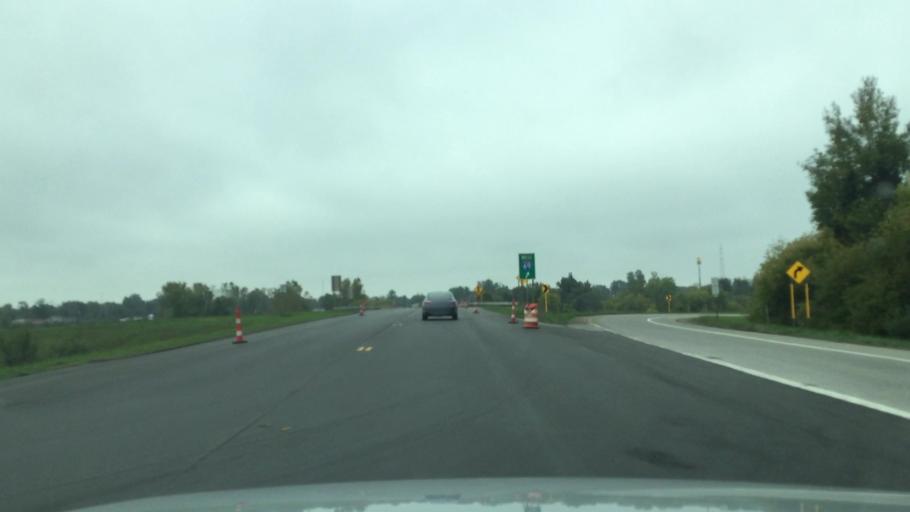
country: US
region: Michigan
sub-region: Shiawassee County
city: Perry
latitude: 42.8421
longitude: -84.2199
